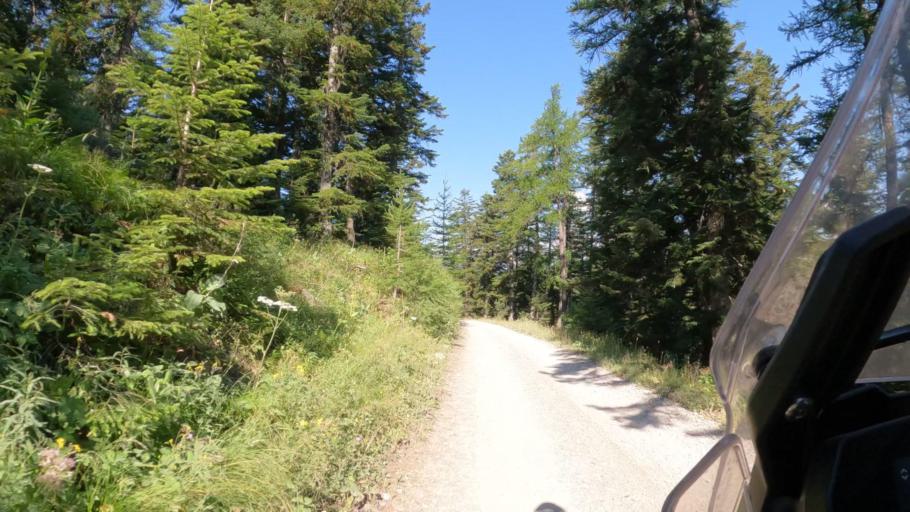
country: FR
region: Provence-Alpes-Cote d'Azur
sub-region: Departement des Hautes-Alpes
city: Embrun
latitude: 44.5947
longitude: 6.5725
